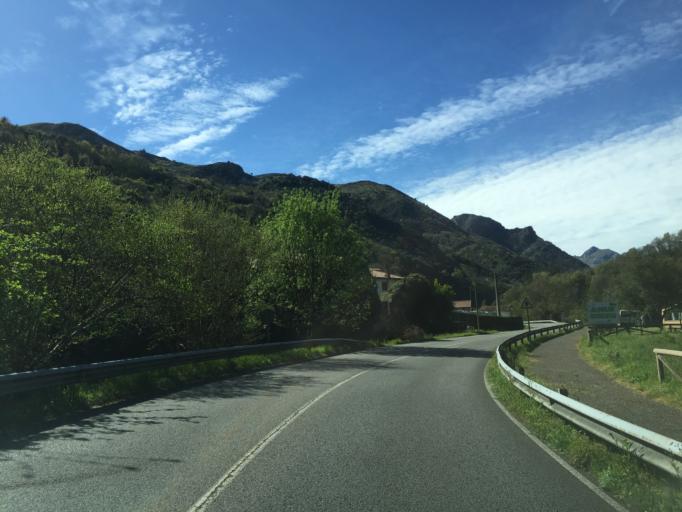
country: ES
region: Asturias
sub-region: Province of Asturias
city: Proaza
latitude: 43.2927
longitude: -5.9818
